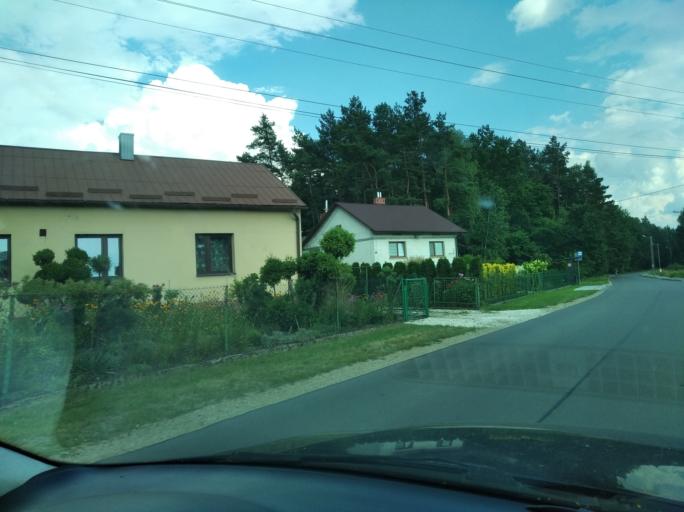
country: PL
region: Subcarpathian Voivodeship
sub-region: Powiat rzeszowski
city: Wysoka Glogowska
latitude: 50.1345
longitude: 22.0208
